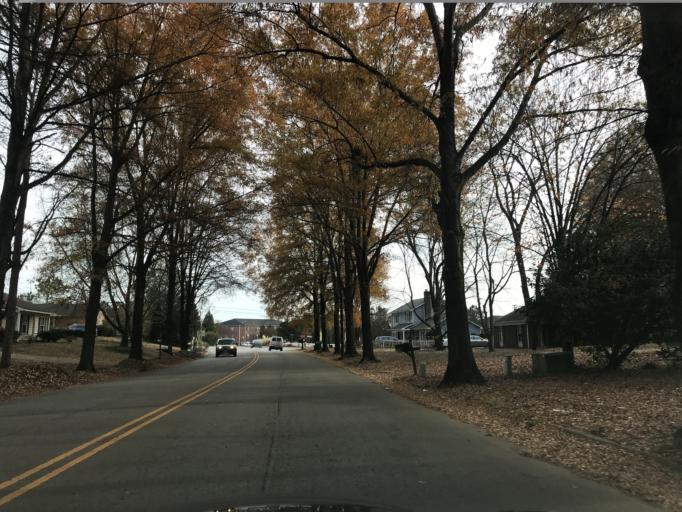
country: US
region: North Carolina
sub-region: Wake County
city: Knightdale
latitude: 35.8491
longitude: -78.5640
